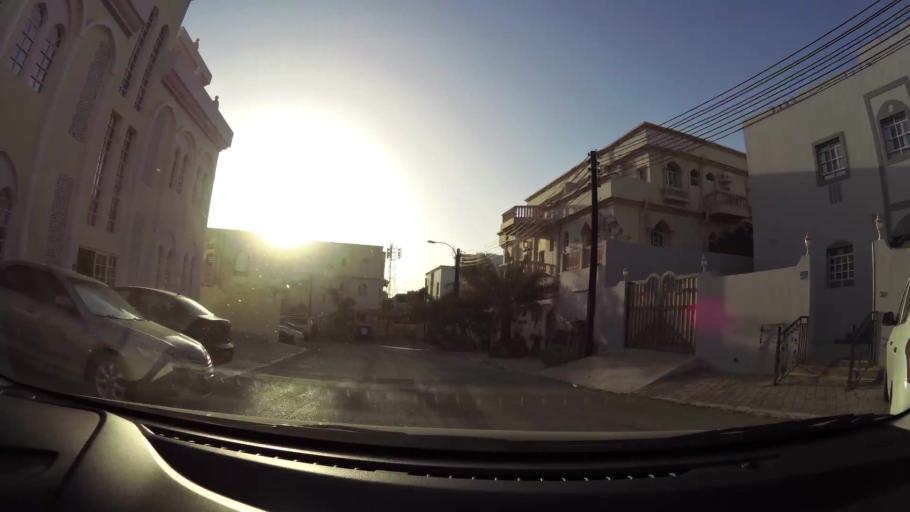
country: OM
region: Muhafazat Masqat
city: Muscat
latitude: 23.5657
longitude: 58.5826
